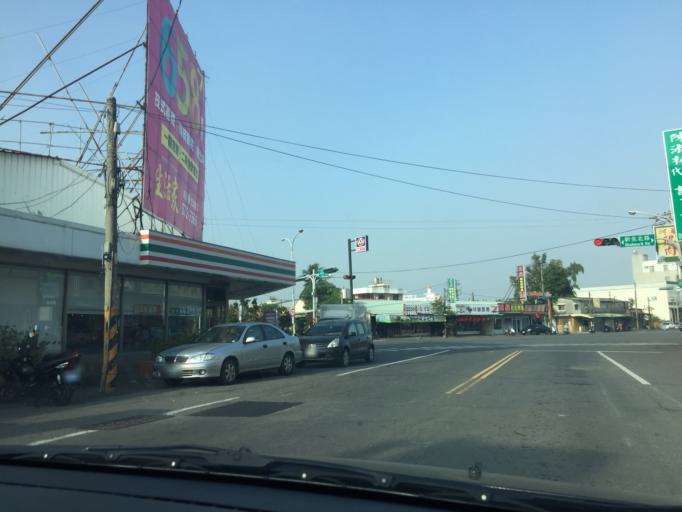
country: TW
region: Taiwan
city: Xinying
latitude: 23.1894
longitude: 120.2529
